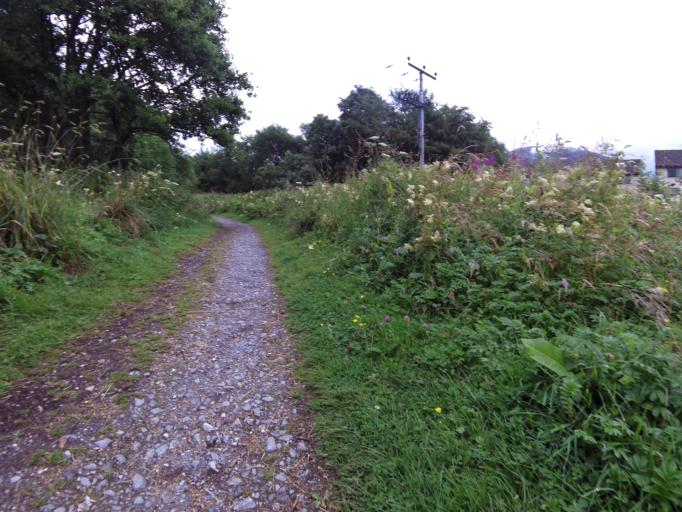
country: GB
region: Scotland
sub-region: Highland
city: Fort William
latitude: 56.8263
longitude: -5.0983
